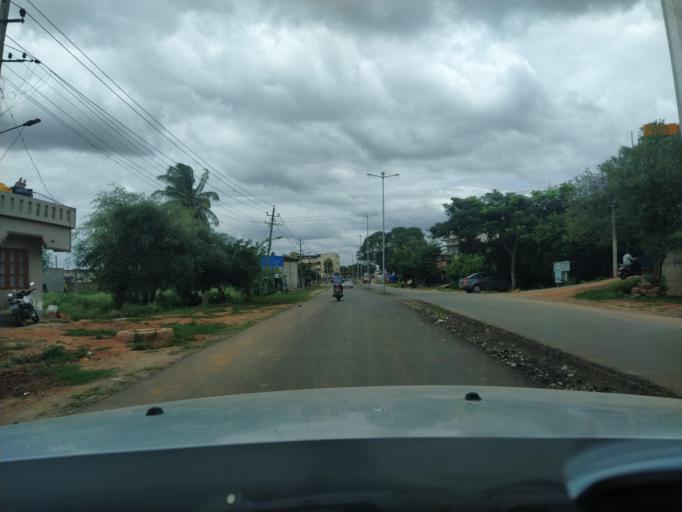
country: IN
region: Karnataka
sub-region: Tumkur
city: Tumkur
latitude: 13.3131
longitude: 77.1357
